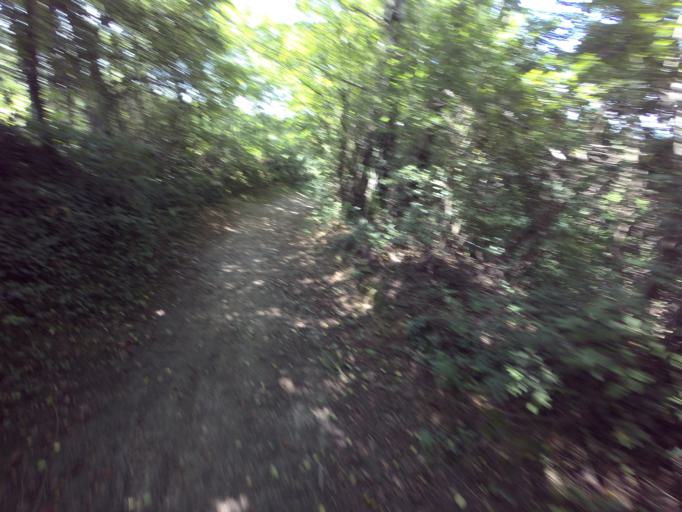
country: BE
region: Wallonia
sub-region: Province de Liege
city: Lontzen
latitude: 50.6932
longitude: 5.9992
